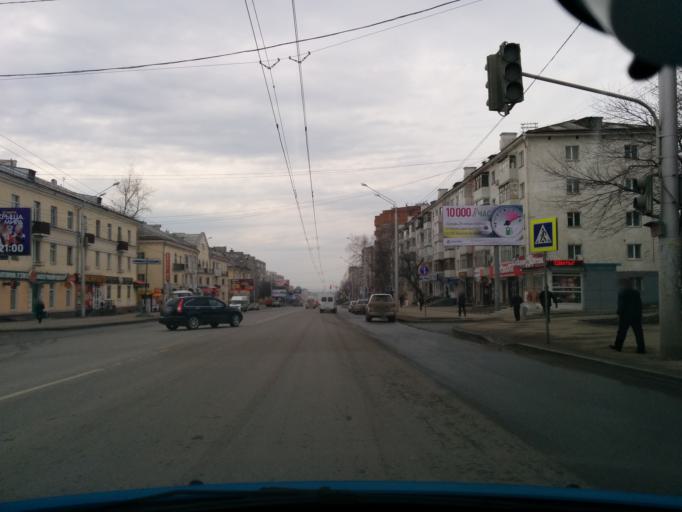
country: RU
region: Bashkortostan
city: Ufa
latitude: 54.7335
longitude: 55.9796
